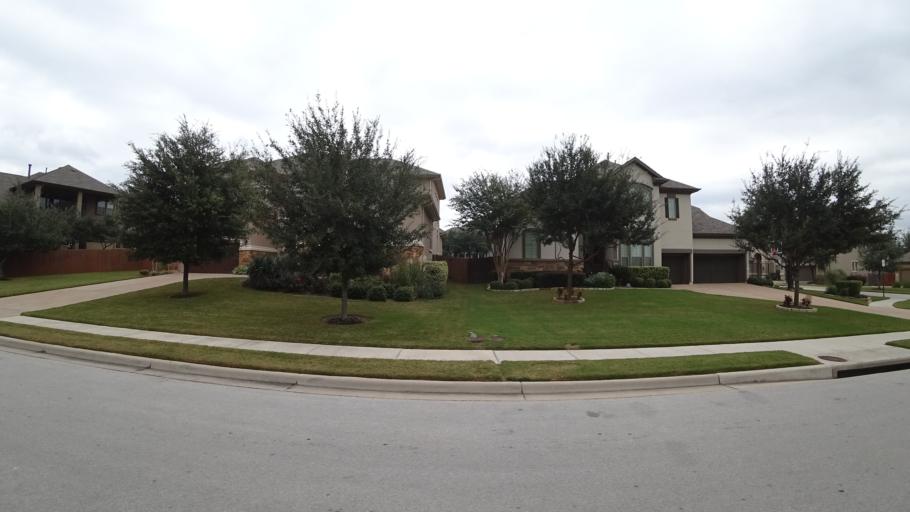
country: US
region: Texas
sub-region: Travis County
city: Bee Cave
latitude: 30.3402
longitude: -97.9133
